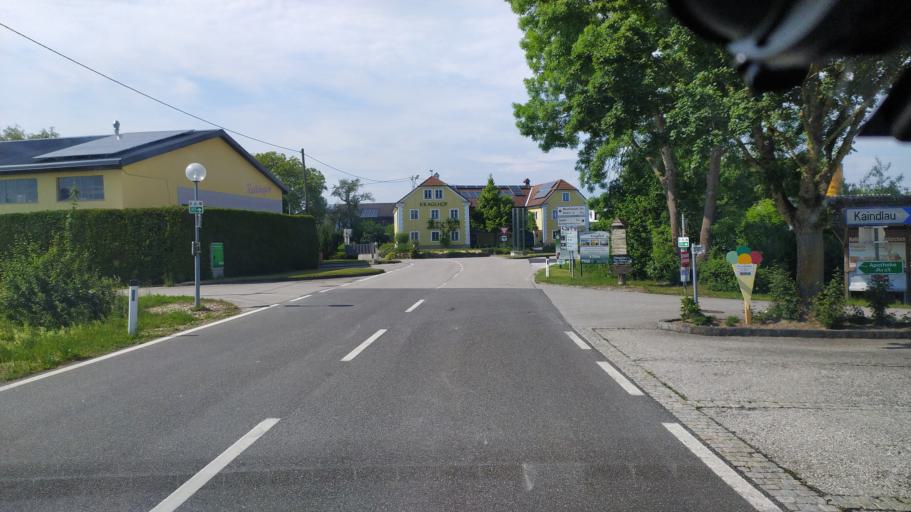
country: AT
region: Lower Austria
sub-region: Politischer Bezirk Amstetten
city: Strengberg
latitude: 48.1843
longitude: 14.7130
